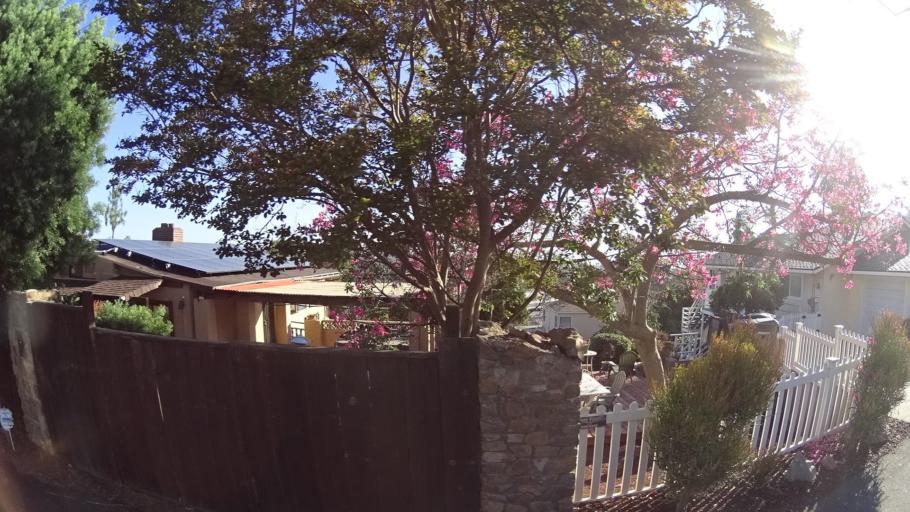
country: US
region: California
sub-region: San Diego County
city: La Mesa
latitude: 32.7779
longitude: -116.9977
